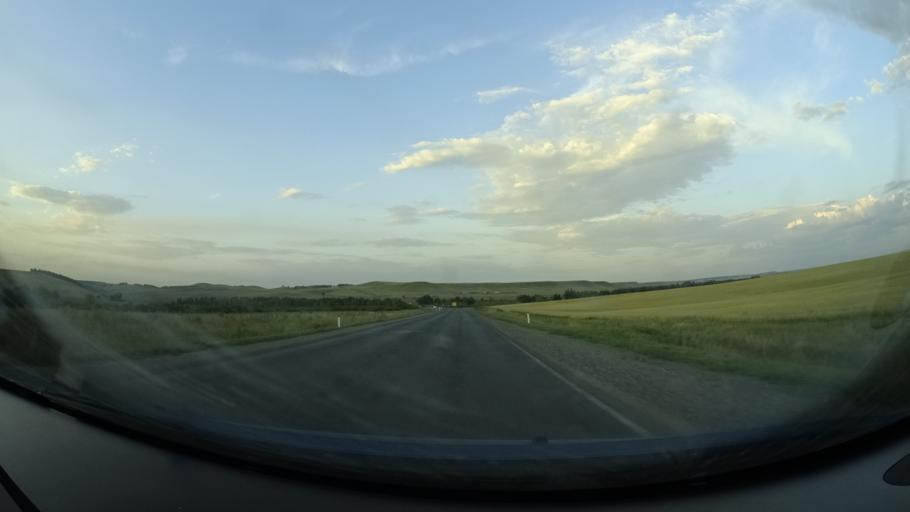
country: RU
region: Orenburg
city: Severnoye
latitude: 54.1308
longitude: 52.5842
